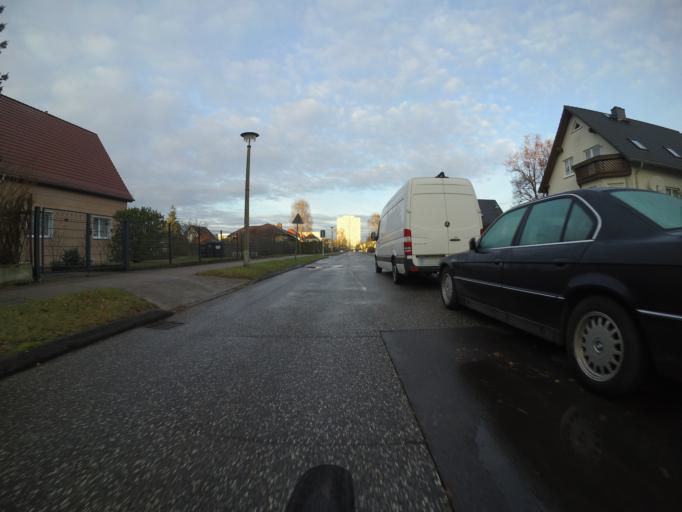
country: DE
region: Berlin
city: Marzahn
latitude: 52.5394
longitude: 13.5507
